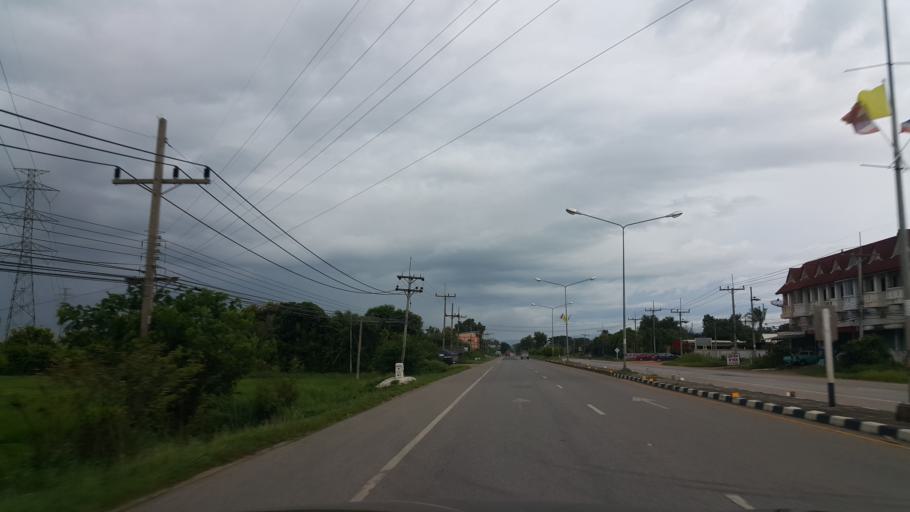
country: TH
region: Phayao
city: Dok Kham Tai
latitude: 19.1460
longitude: 99.9284
